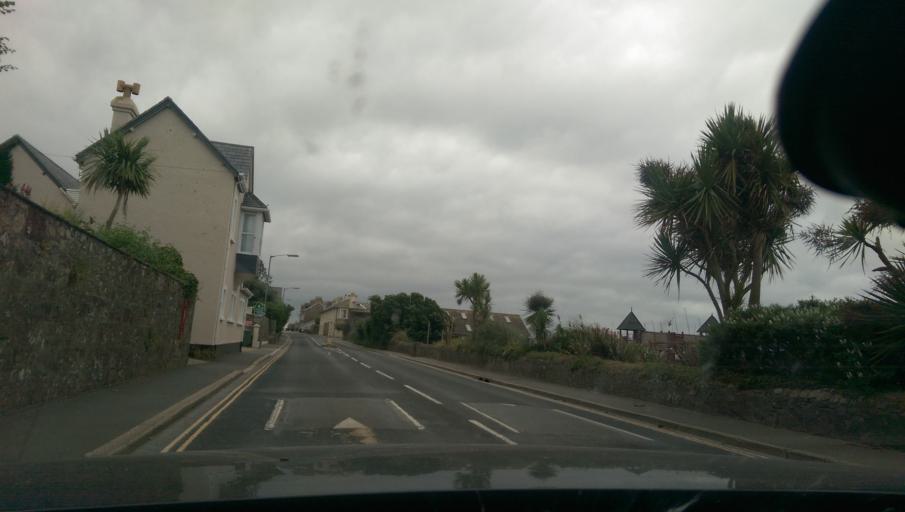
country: GB
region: England
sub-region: Cornwall
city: Marazion
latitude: 50.1255
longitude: -5.4772
